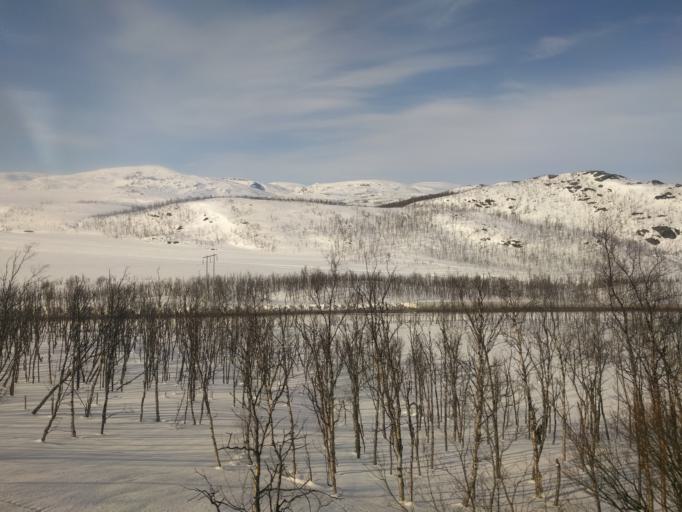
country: NO
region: Troms
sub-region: Bardu
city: Setermoen
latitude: 68.4255
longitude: 18.4289
